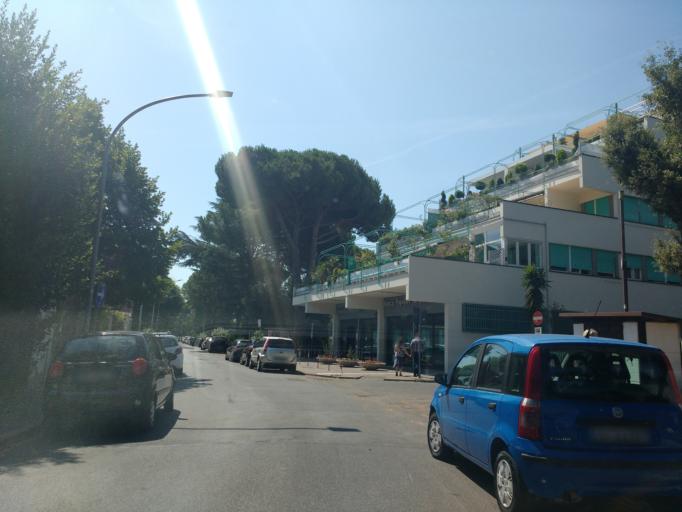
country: IT
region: Latium
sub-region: Citta metropolitana di Roma Capitale
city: Acilia-Castel Fusano-Ostia Antica
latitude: 41.7525
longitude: 12.3549
